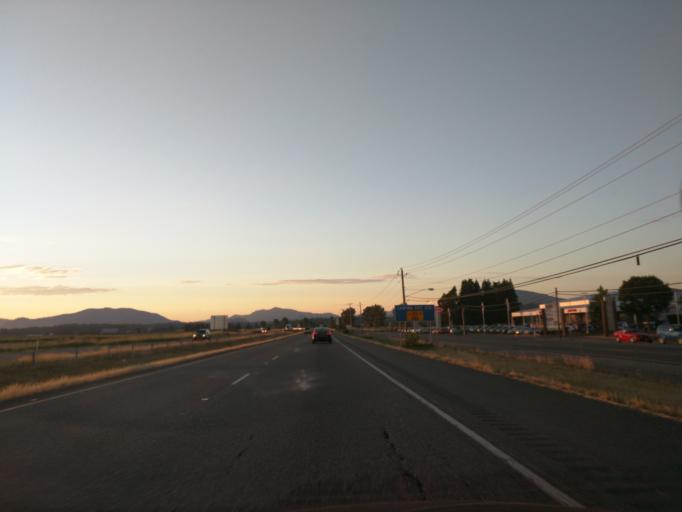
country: US
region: Washington
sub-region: Skagit County
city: Burlington
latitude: 48.4909
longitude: -122.3355
